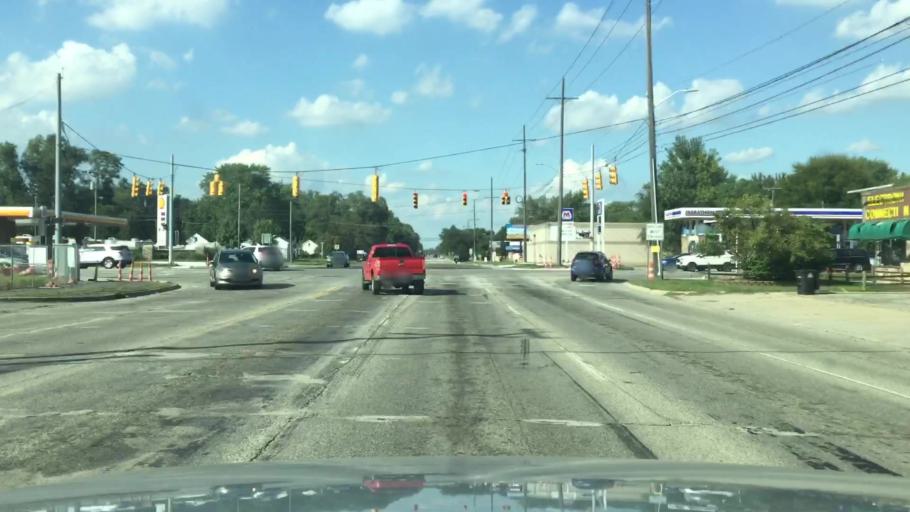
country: US
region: Michigan
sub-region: Wayne County
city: Westland
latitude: 42.3235
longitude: -83.4086
